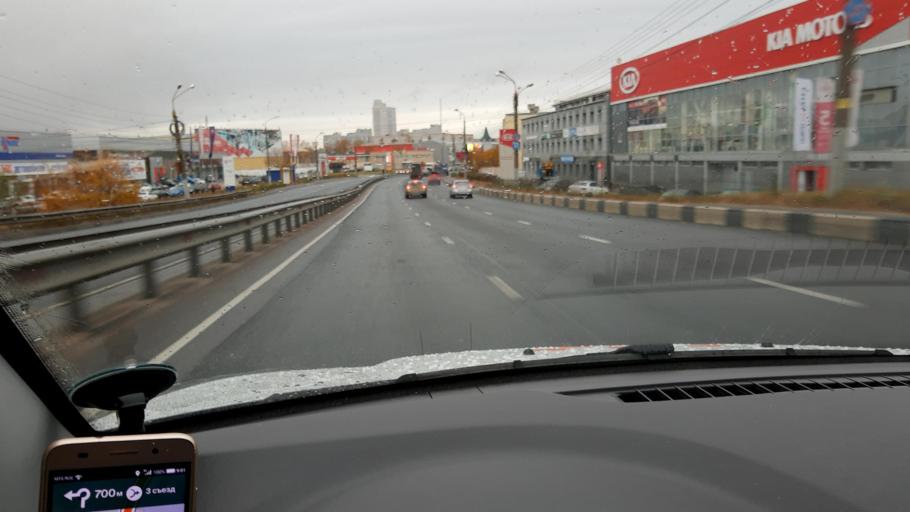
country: RU
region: Nizjnij Novgorod
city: Nizhniy Novgorod
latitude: 56.3097
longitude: 43.9034
